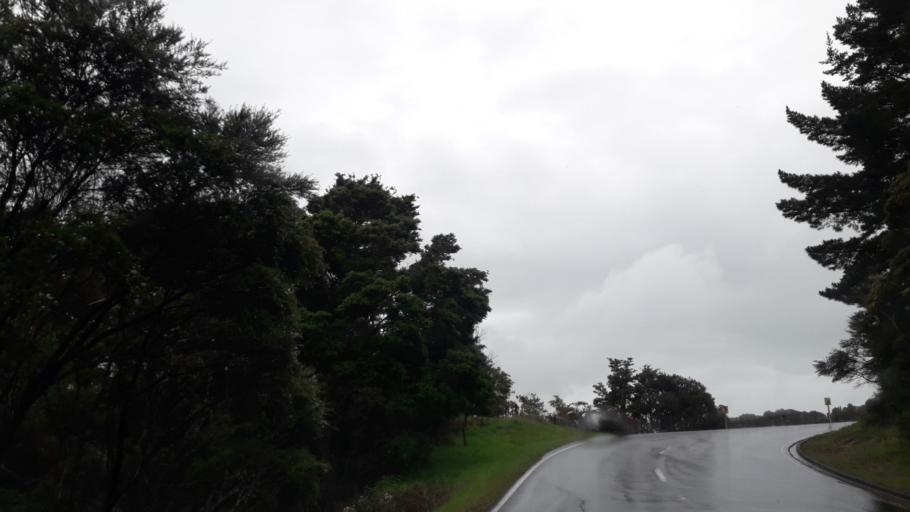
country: NZ
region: Northland
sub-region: Far North District
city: Kaitaia
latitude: -35.3571
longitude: 173.4872
